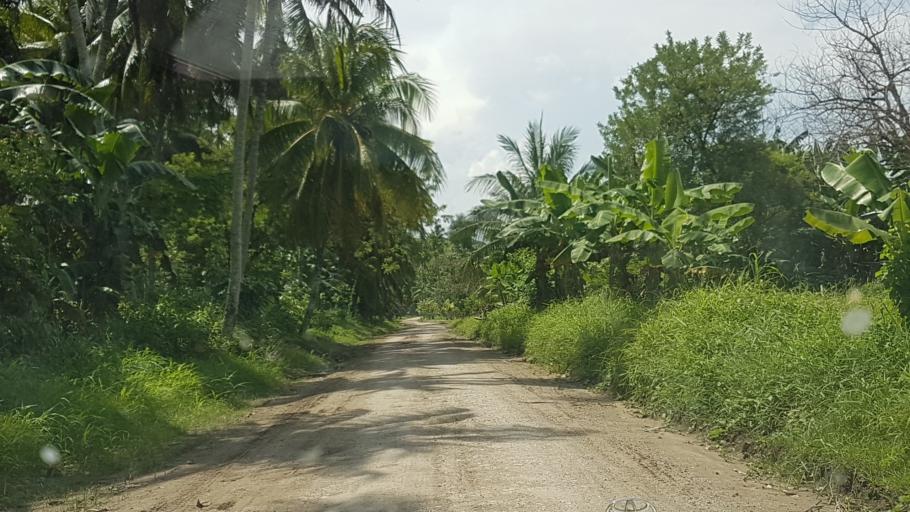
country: PG
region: East Sepik
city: Angoram
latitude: -4.2325
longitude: 144.9400
